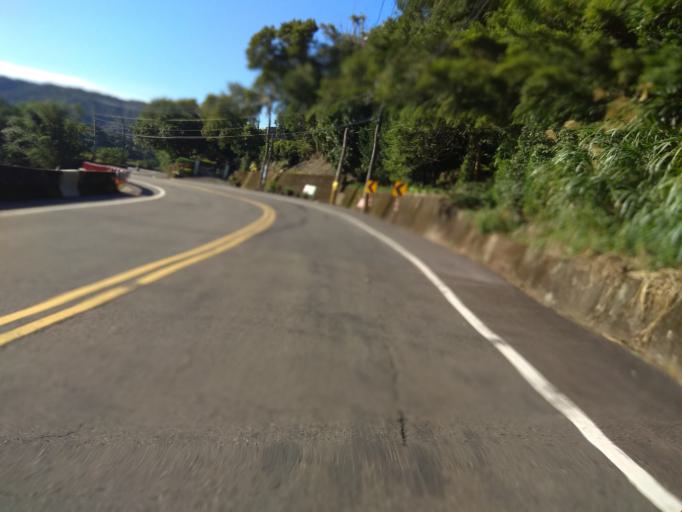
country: TW
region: Taiwan
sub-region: Hsinchu
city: Zhubei
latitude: 24.8513
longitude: 121.1458
